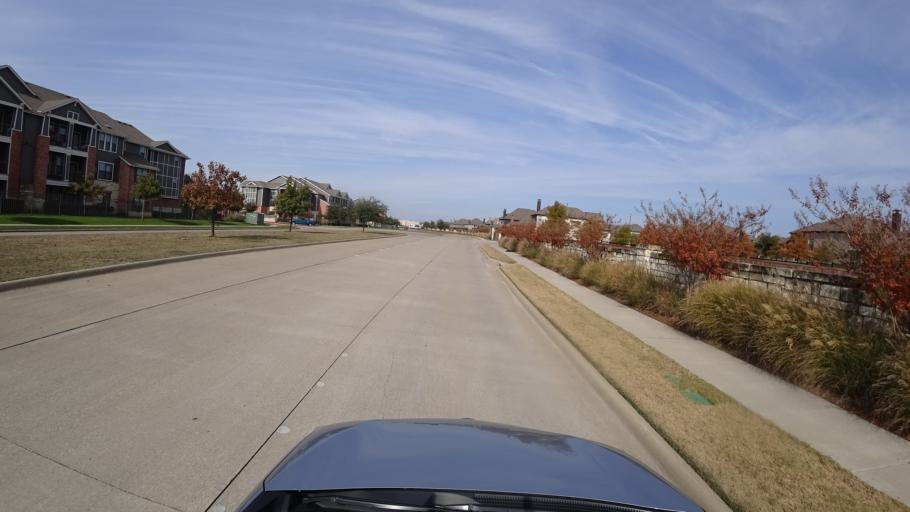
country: US
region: Texas
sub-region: Denton County
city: The Colony
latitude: 33.0616
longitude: -96.8783
